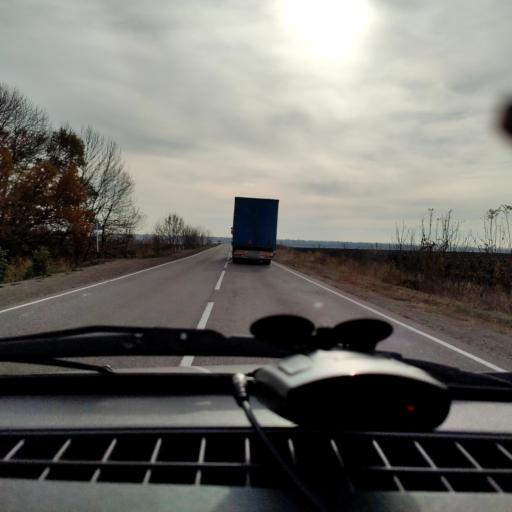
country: RU
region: Voronezj
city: Shilovo
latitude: 51.4568
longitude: 38.9724
